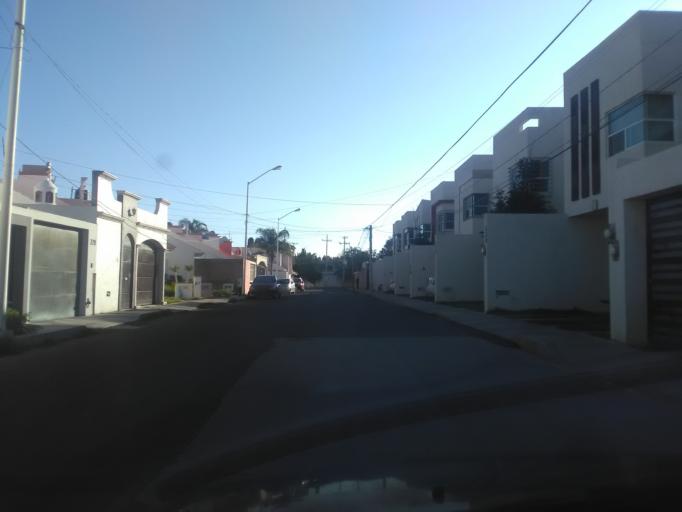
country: MX
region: Durango
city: Victoria de Durango
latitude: 24.0002
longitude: -104.7034
